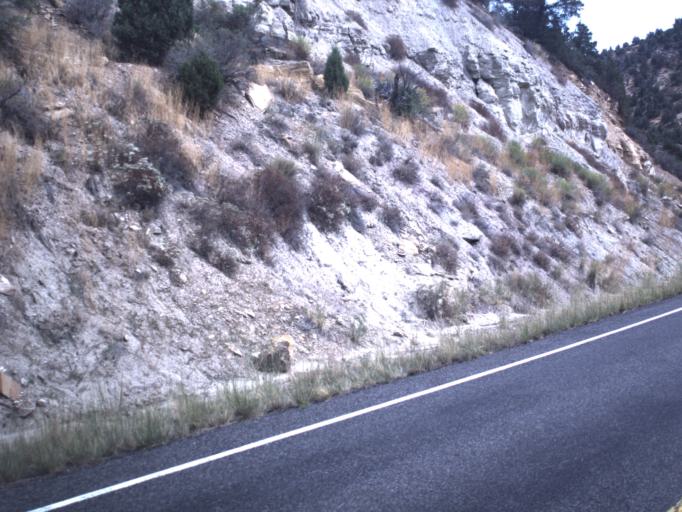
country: US
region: Utah
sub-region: Kane County
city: Kanab
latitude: 37.3626
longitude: -112.5947
